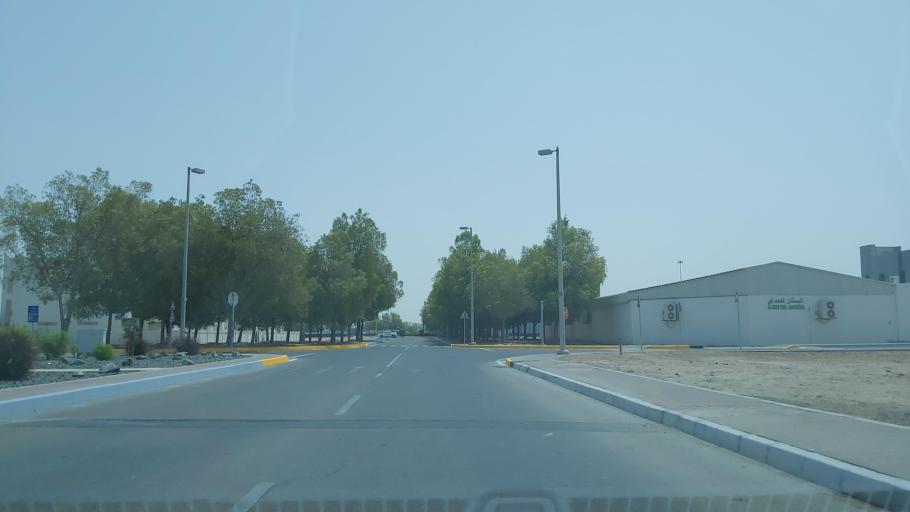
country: AE
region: Abu Dhabi
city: Abu Dhabi
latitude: 24.3794
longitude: 54.5215
